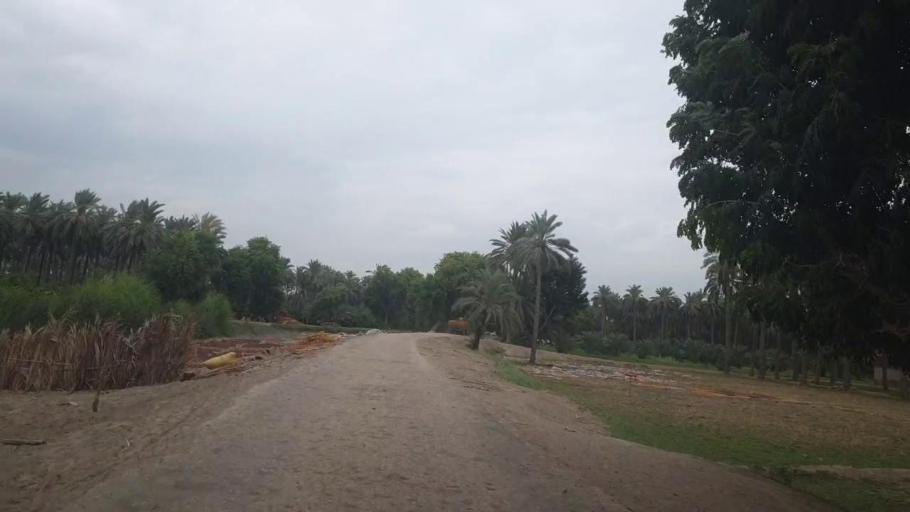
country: PK
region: Sindh
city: Khairpur
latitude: 27.6034
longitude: 68.7610
